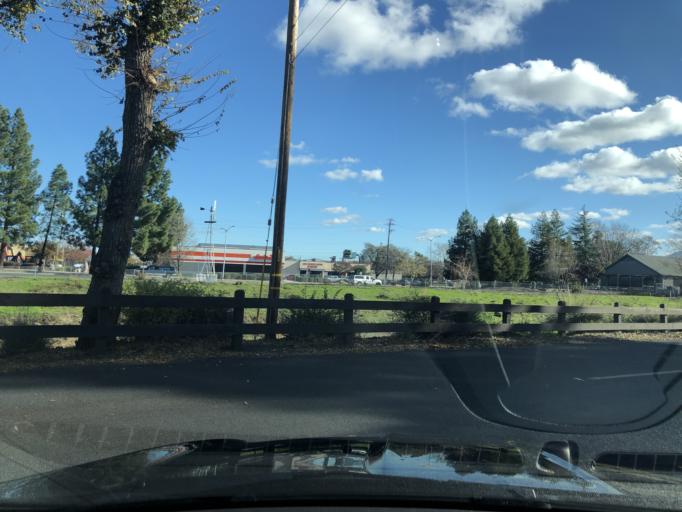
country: US
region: California
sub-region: Contra Costa County
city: Pacheco
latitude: 37.9857
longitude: -122.0695
